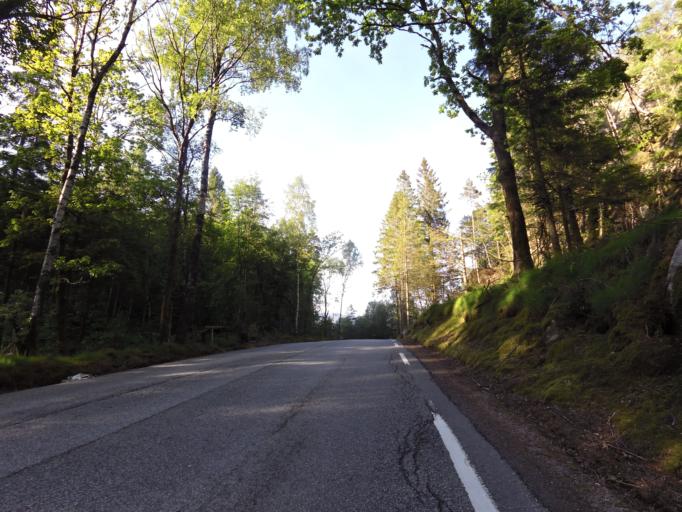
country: NO
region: Vest-Agder
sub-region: Flekkefjord
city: Flekkefjord
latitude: 58.2788
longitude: 6.6385
